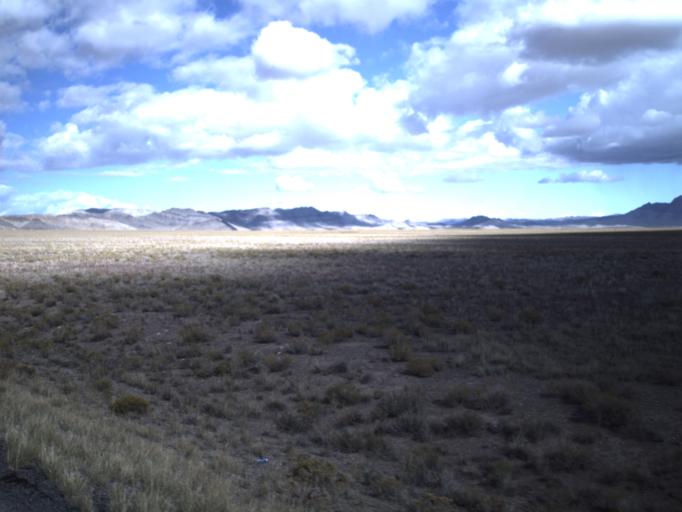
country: US
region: Utah
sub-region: Beaver County
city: Milford
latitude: 38.5554
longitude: -113.7442
